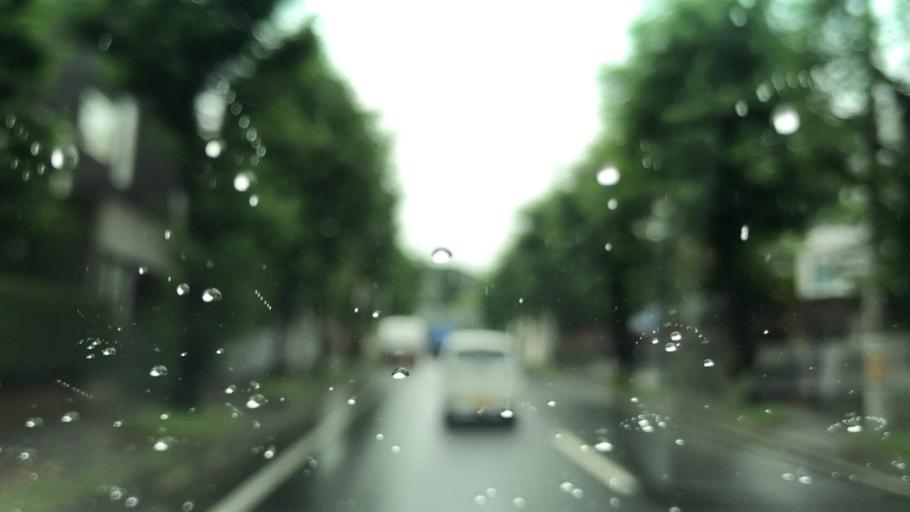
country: JP
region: Hokkaido
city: Sapporo
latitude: 43.0550
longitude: 141.2995
